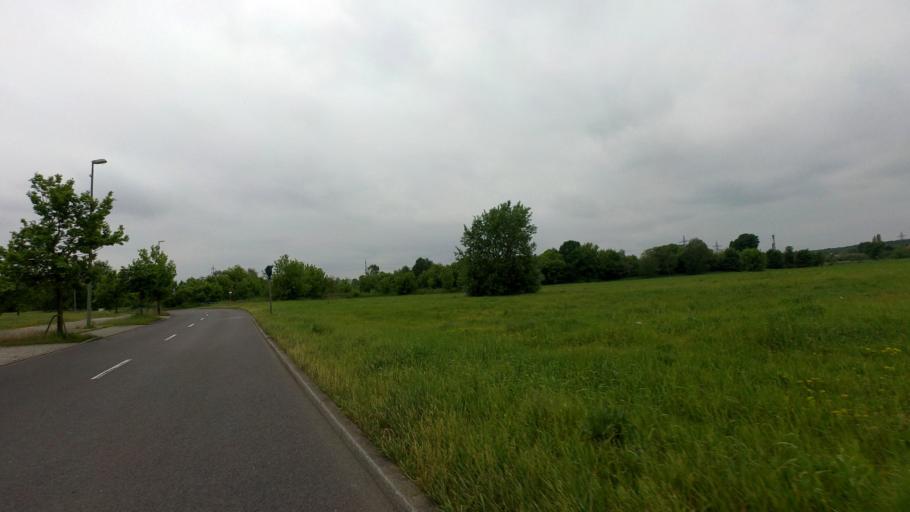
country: DE
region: Berlin
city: Buchholz
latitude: 52.6309
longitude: 13.4341
